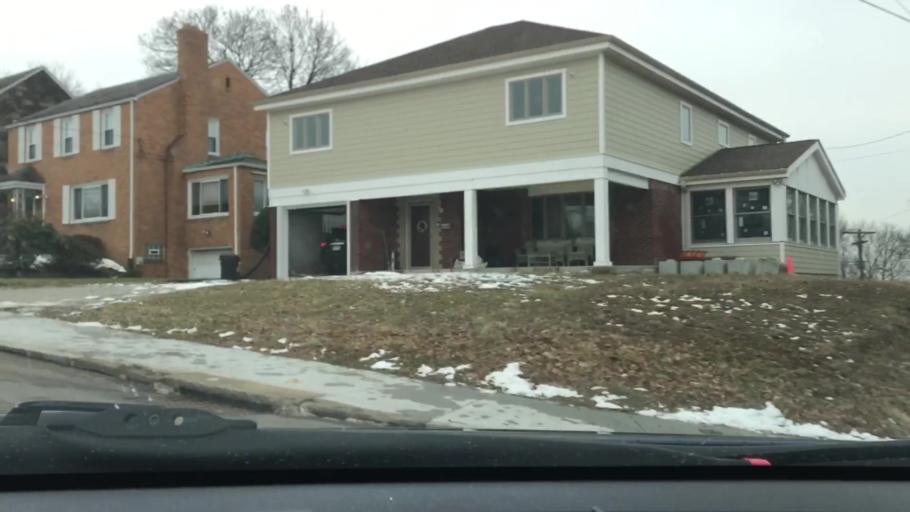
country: US
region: Pennsylvania
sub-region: Allegheny County
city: Ingram
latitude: 40.4516
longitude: -80.0692
